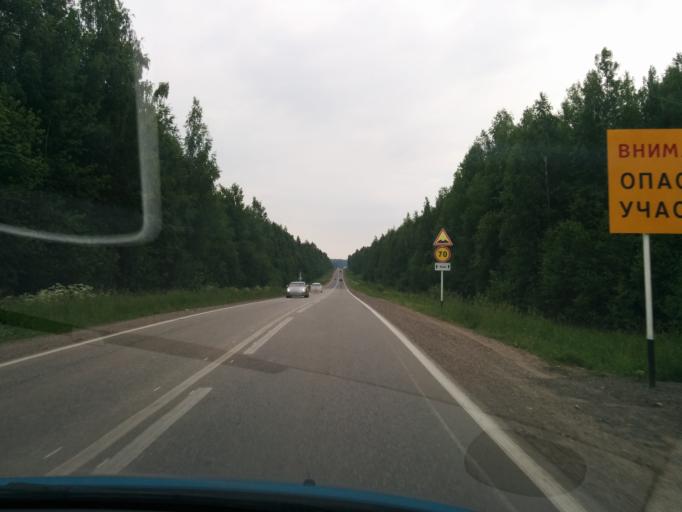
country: RU
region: Perm
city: Perm
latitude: 58.1462
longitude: 56.2621
